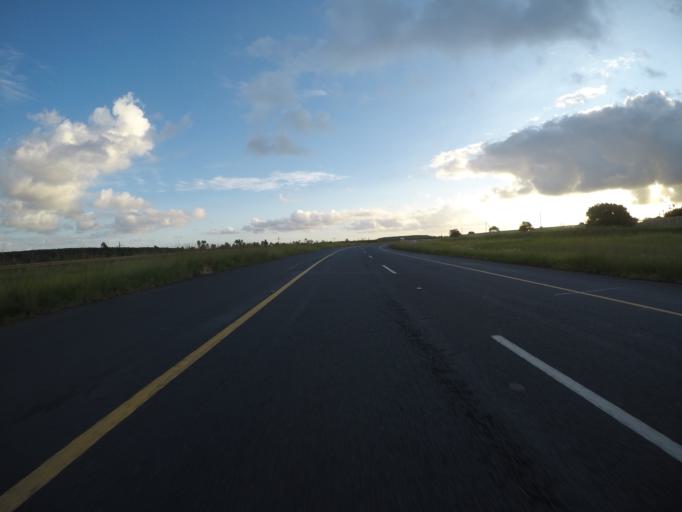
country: ZA
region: KwaZulu-Natal
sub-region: uThungulu District Municipality
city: KwaMbonambi
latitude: -28.6016
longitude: 32.0962
